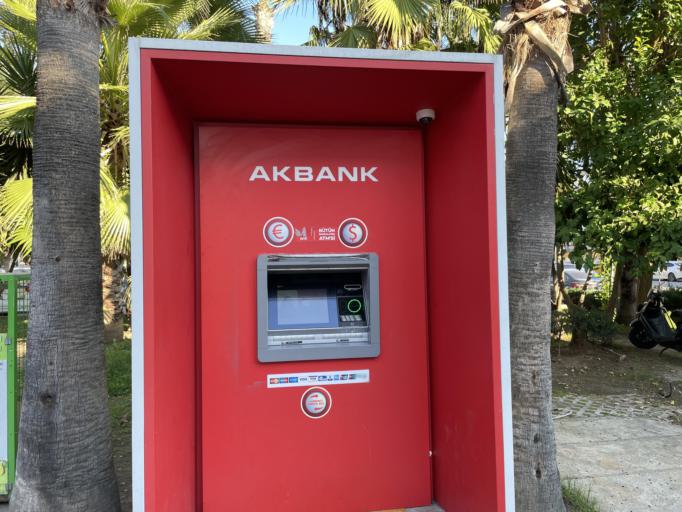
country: TR
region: Antalya
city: Kemer
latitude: 36.5994
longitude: 30.5675
